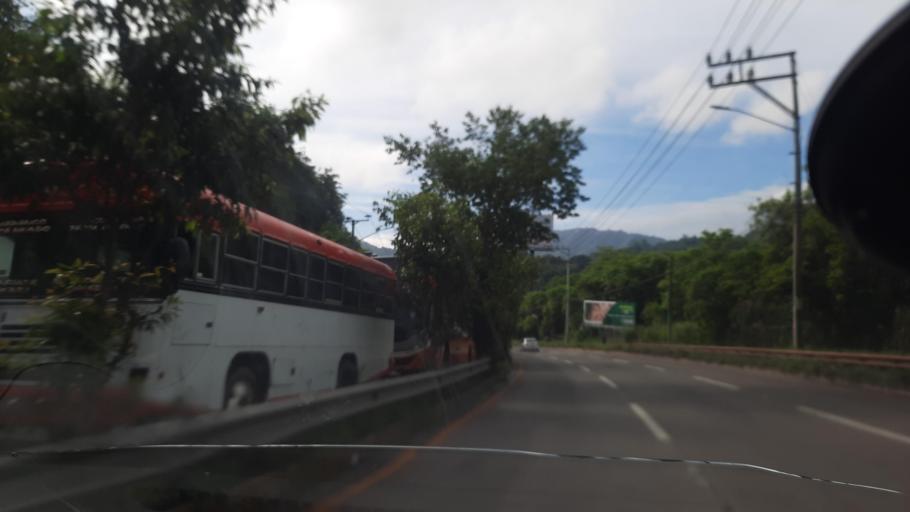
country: SV
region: San Salvador
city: San Salvador
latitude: 13.6752
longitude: -89.2049
